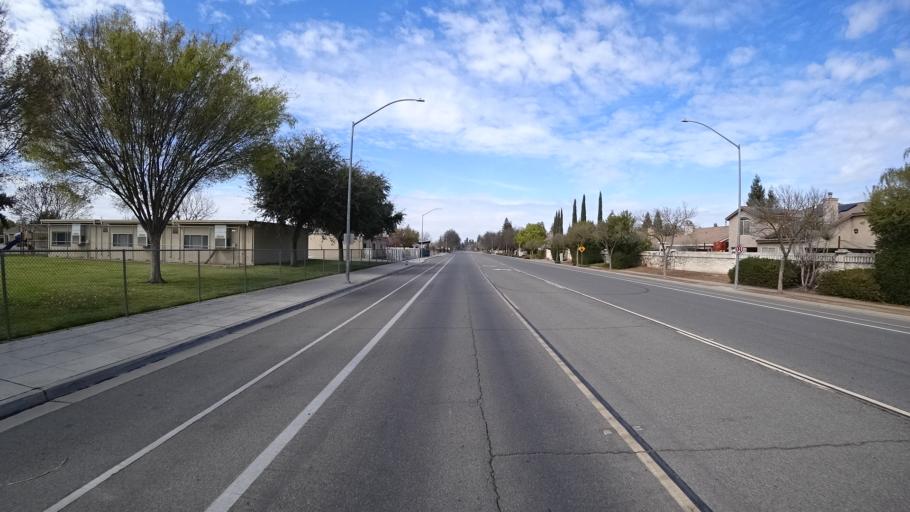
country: US
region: California
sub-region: Fresno County
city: Biola
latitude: 36.8442
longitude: -119.8862
